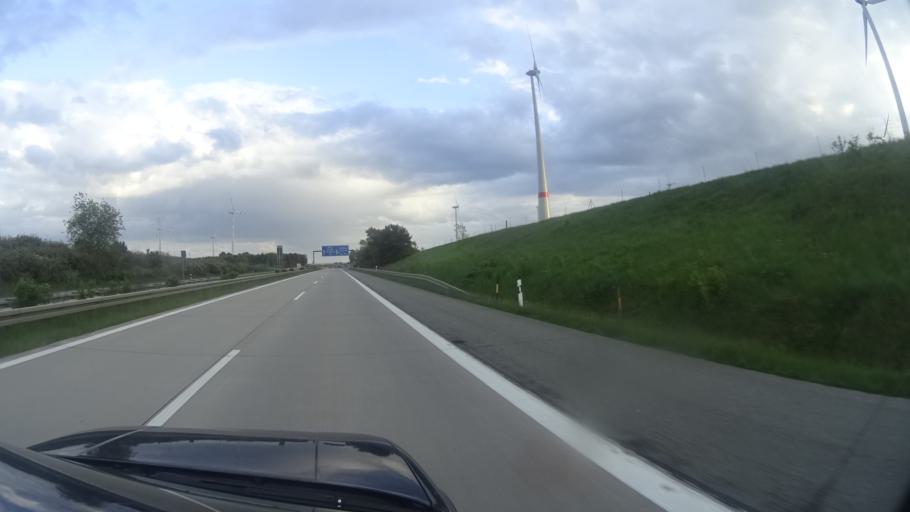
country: DE
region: Brandenburg
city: Wittstock
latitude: 53.1456
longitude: 12.4523
